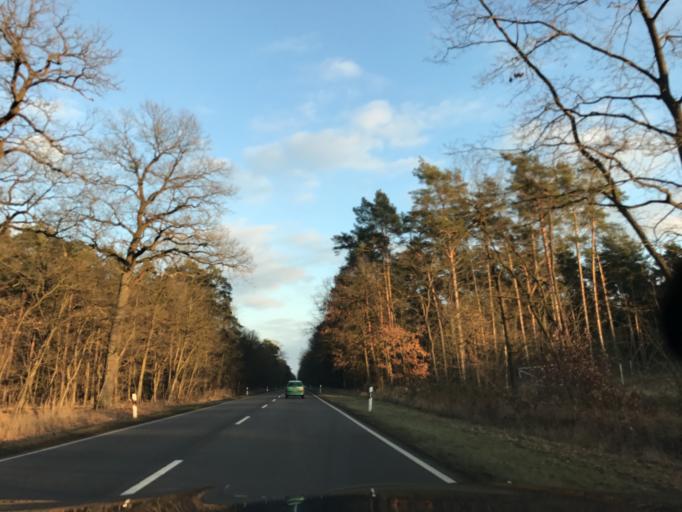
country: DE
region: Brandenburg
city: Bensdorf
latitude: 52.4114
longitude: 12.2595
